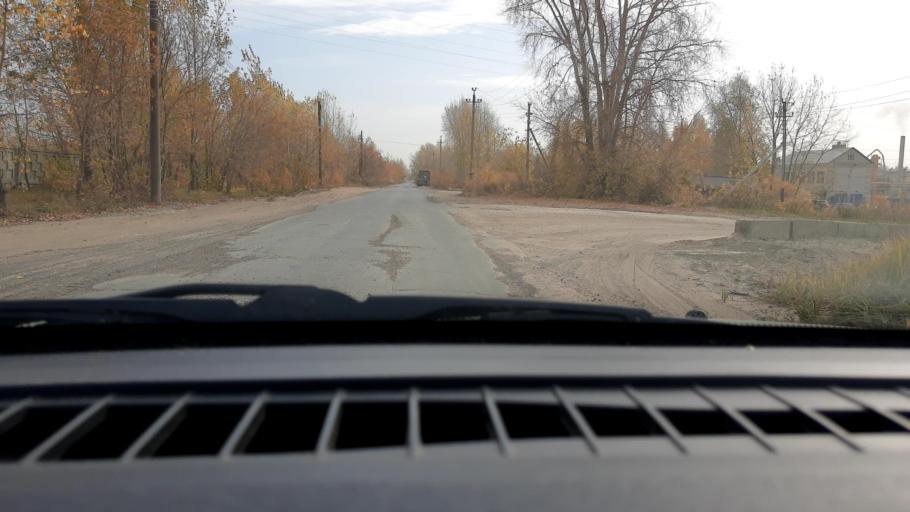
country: RU
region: Nizjnij Novgorod
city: Afonino
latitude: 56.2932
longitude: 44.1110
